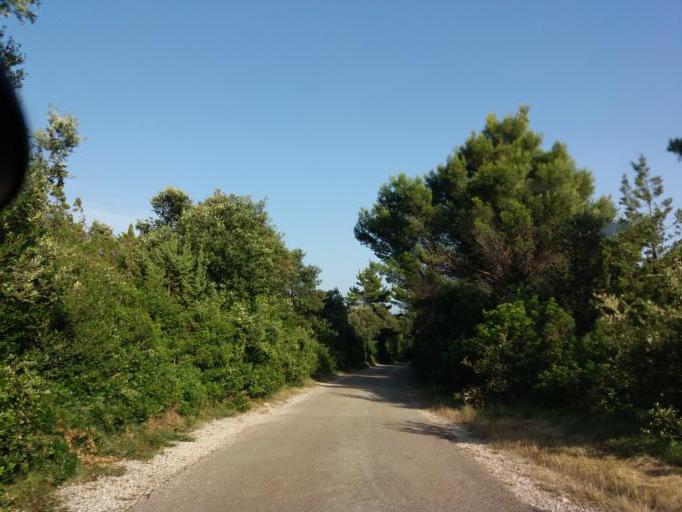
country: HR
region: Zadarska
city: Ugljan
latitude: 44.1488
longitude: 14.8310
